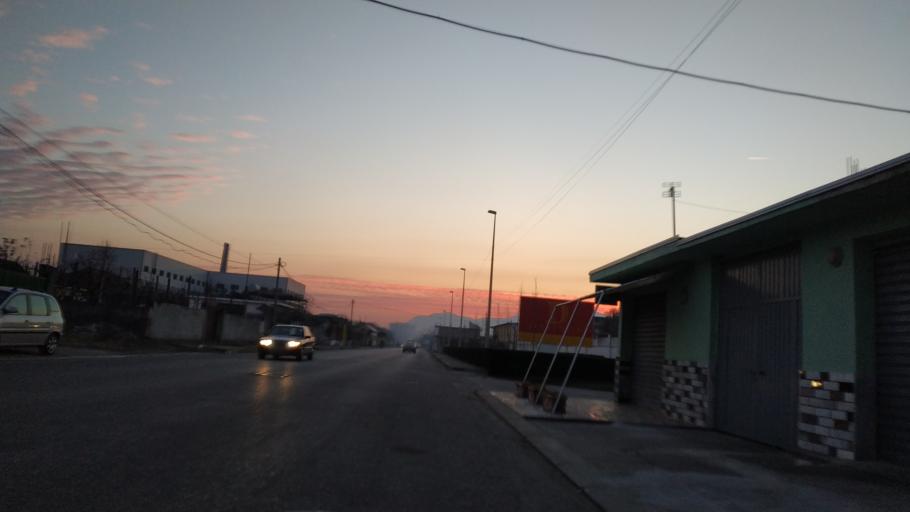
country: AL
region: Shkoder
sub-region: Rrethi i Shkodres
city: Shkoder
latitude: 42.0838
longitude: 19.5286
